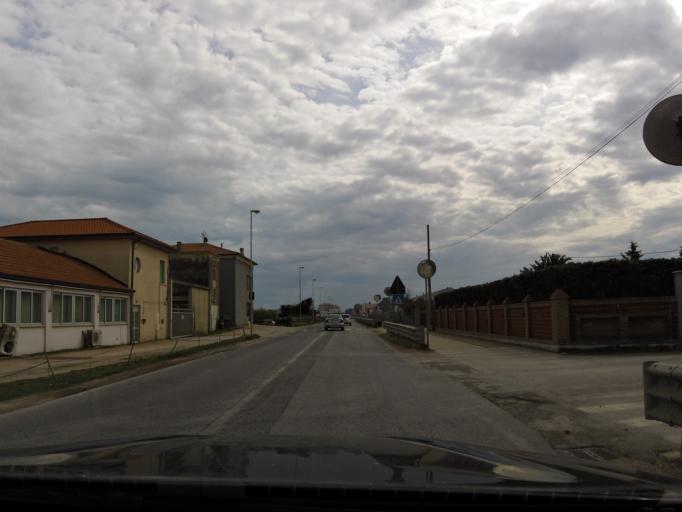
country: IT
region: The Marches
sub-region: Provincia di Macerata
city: Porto Potenza Picena
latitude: 43.3781
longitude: 13.6894
